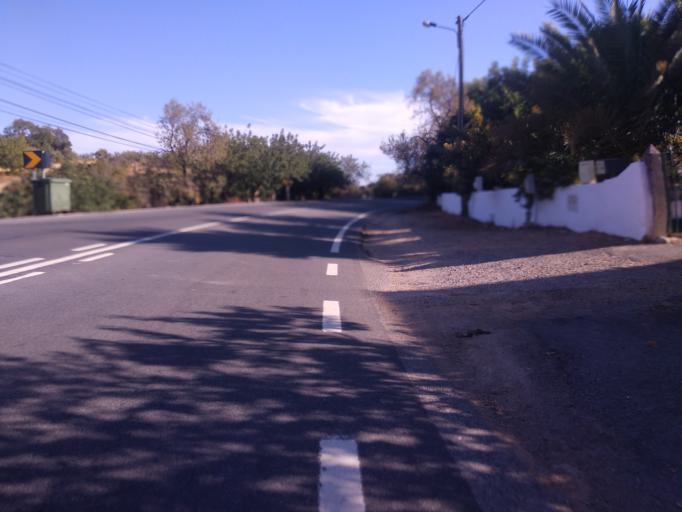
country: PT
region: Faro
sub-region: Sao Bras de Alportel
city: Sao Bras de Alportel
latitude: 37.1071
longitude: -7.9071
